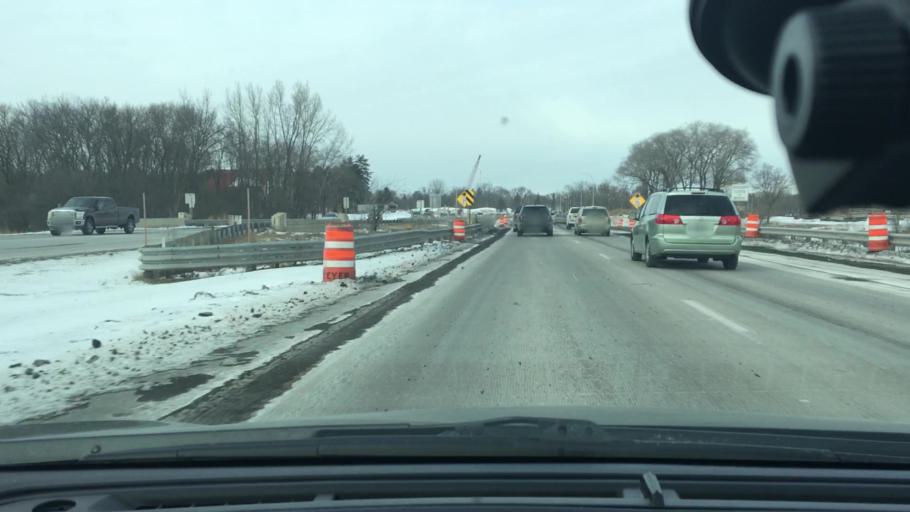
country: US
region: Minnesota
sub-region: Hennepin County
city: Champlin
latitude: 45.1815
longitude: -93.3921
